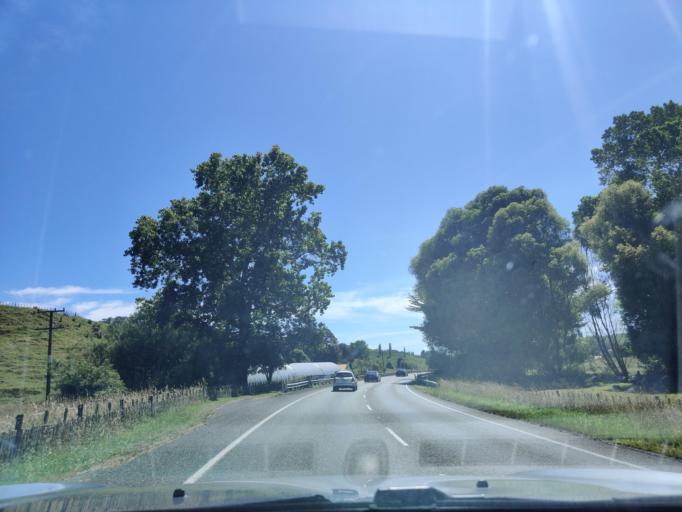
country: NZ
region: Manawatu-Wanganui
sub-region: Rangitikei District
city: Bulls
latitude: -39.9284
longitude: 175.5780
